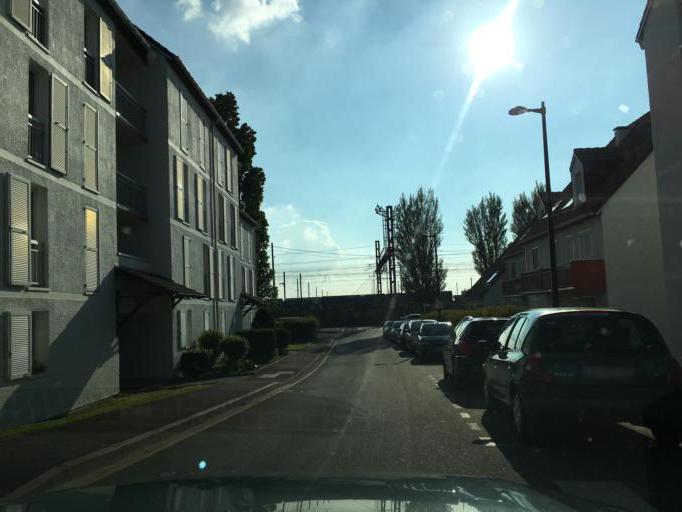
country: FR
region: Centre
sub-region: Departement du Loiret
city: Fleury-les-Aubrais
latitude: 47.9329
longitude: 1.9049
